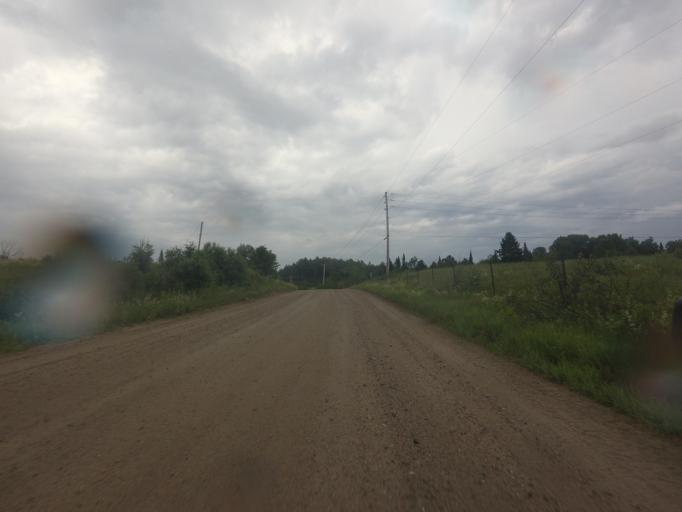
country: CA
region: Quebec
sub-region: Outaouais
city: Maniwaki
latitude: 46.4491
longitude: -75.9406
